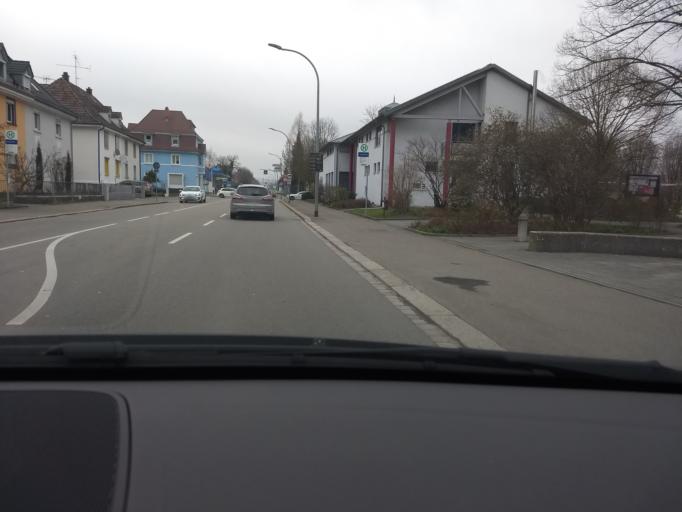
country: DE
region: Baden-Wuerttemberg
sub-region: Freiburg Region
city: Rheinfelden (Baden)
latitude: 47.5616
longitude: 7.7912
